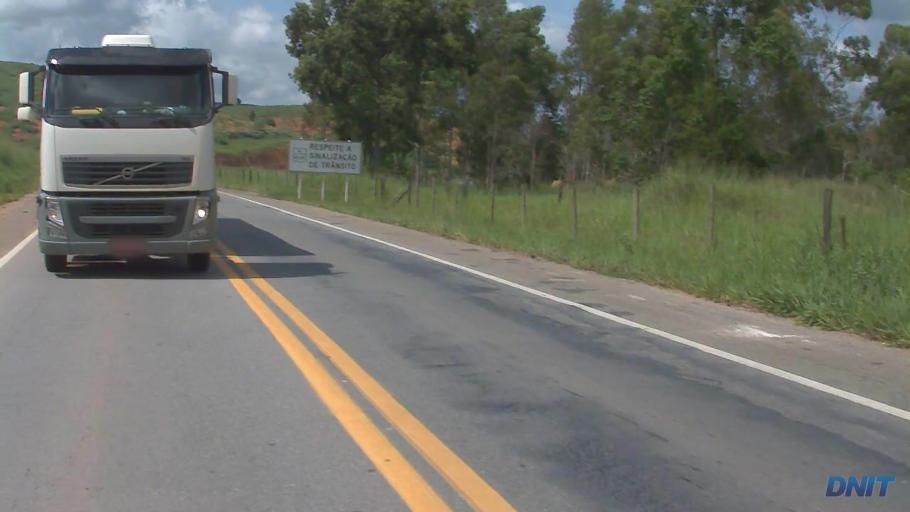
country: BR
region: Minas Gerais
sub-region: Governador Valadares
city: Governador Valadares
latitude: -19.0644
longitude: -42.1633
